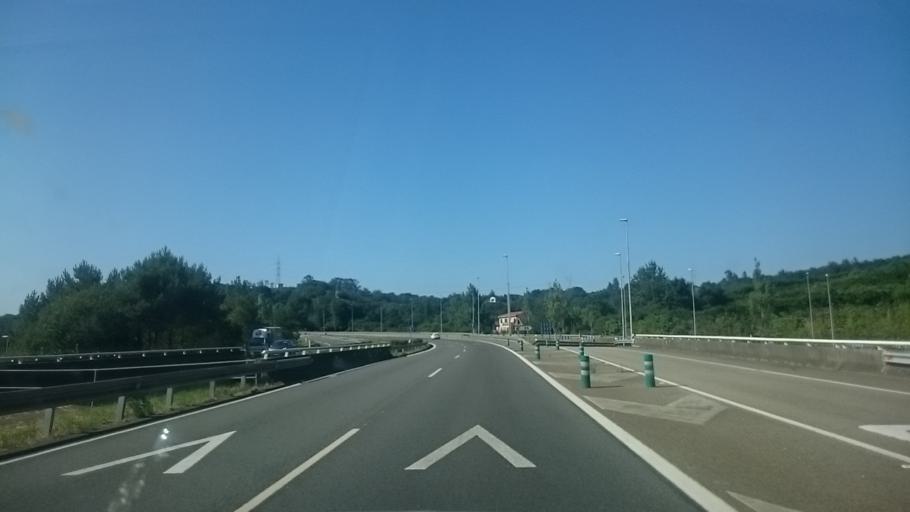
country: ES
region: Asturias
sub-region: Province of Asturias
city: Castandiello
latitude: 43.3143
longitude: -5.8678
